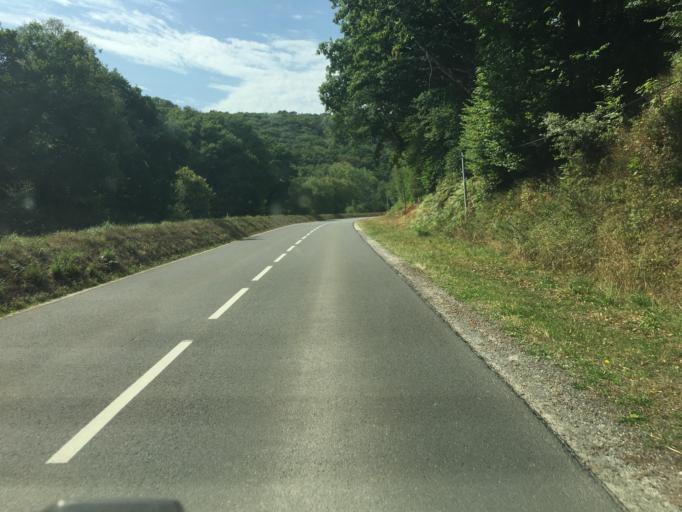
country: FR
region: Brittany
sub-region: Departement des Cotes-d'Armor
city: Gouarec
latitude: 48.2143
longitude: -3.1562
